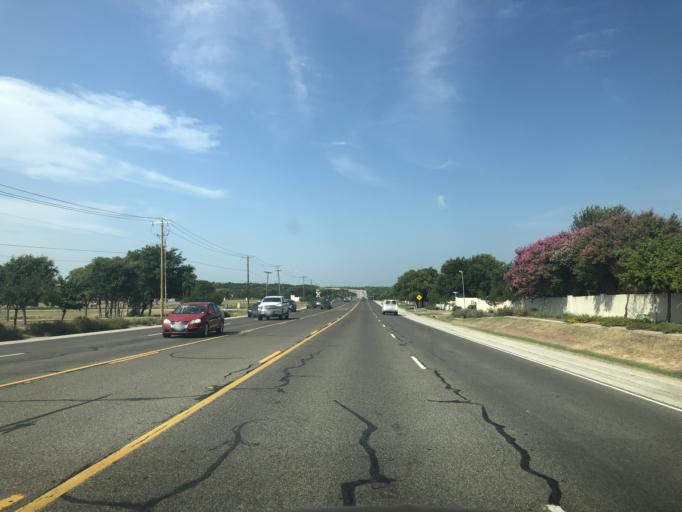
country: US
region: Texas
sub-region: Tarrant County
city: Benbrook
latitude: 32.6655
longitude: -97.4800
